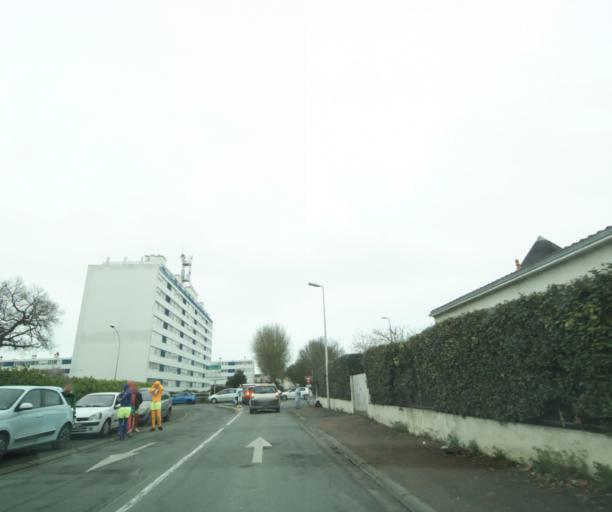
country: FR
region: Poitou-Charentes
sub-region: Departement de la Charente-Maritime
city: Puilboreau
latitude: 46.1726
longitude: -1.1239
